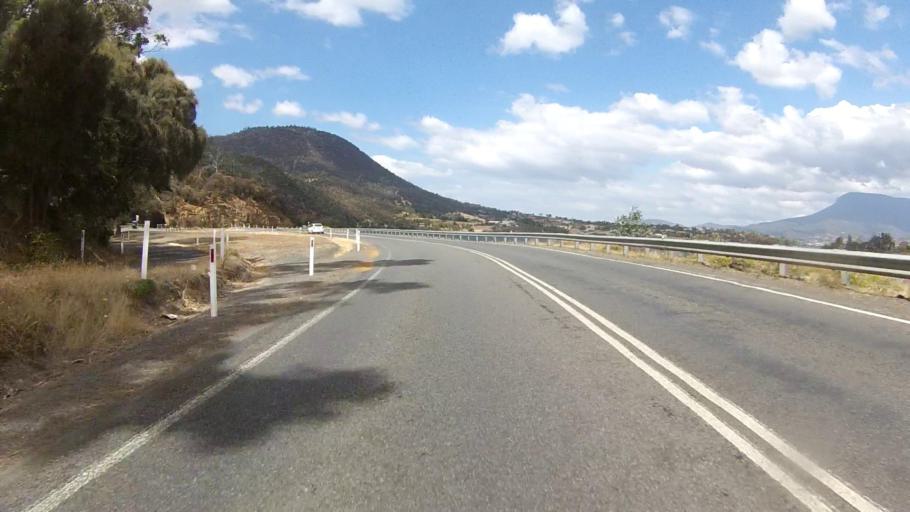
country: AU
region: Tasmania
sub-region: Brighton
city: Old Beach
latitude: -42.7823
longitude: 147.2859
